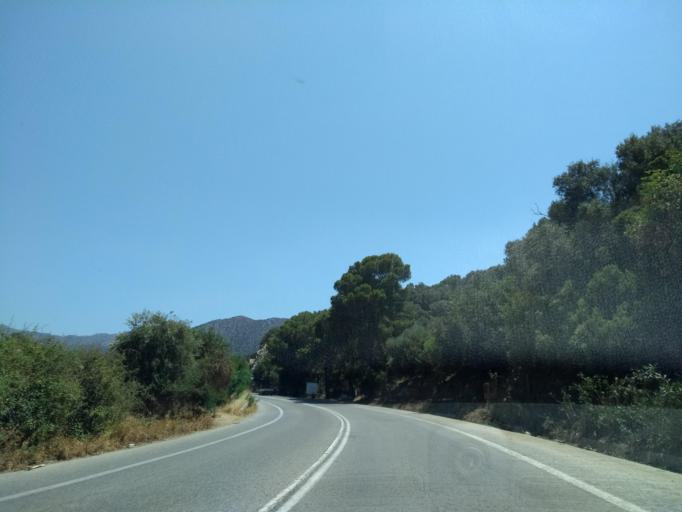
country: GR
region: Crete
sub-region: Nomos Irakleiou
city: Tilisos
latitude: 35.3970
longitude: 24.9489
